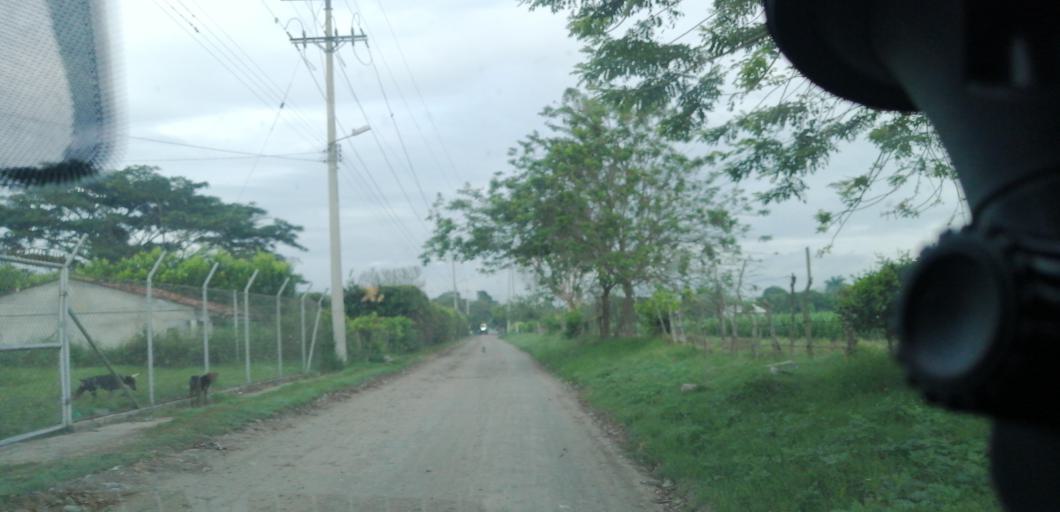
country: CO
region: Valle del Cauca
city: Yumbo
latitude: 3.5721
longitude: -76.3999
